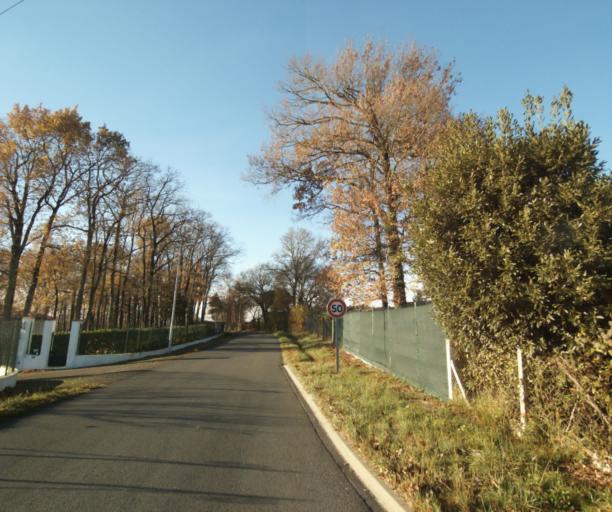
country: FR
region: Poitou-Charentes
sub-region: Departement de la Charente-Maritime
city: Fontcouverte
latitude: 45.7653
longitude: -0.6108
